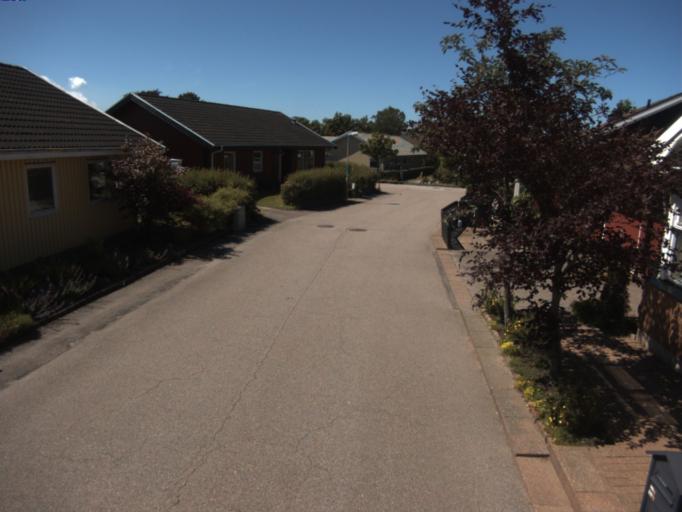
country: SE
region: Skane
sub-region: Helsingborg
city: Glumslov
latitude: 55.9613
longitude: 12.8590
